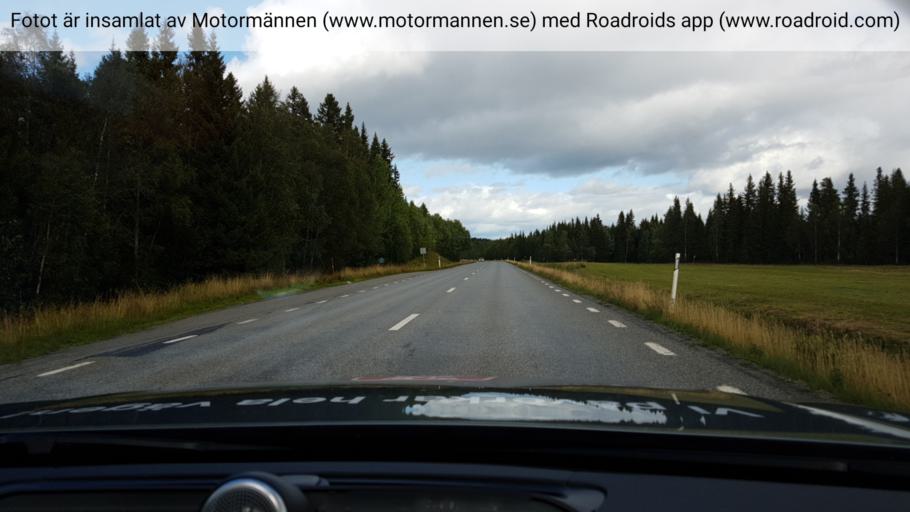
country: SE
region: Jaemtland
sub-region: OEstersunds Kommun
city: Lit
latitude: 63.4240
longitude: 15.1126
